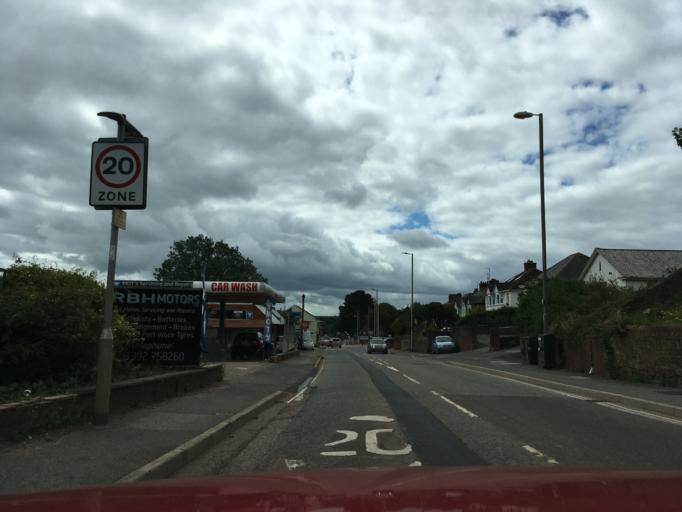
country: GB
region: England
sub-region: Devon
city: Heavitree
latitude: 50.7416
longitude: -3.4684
